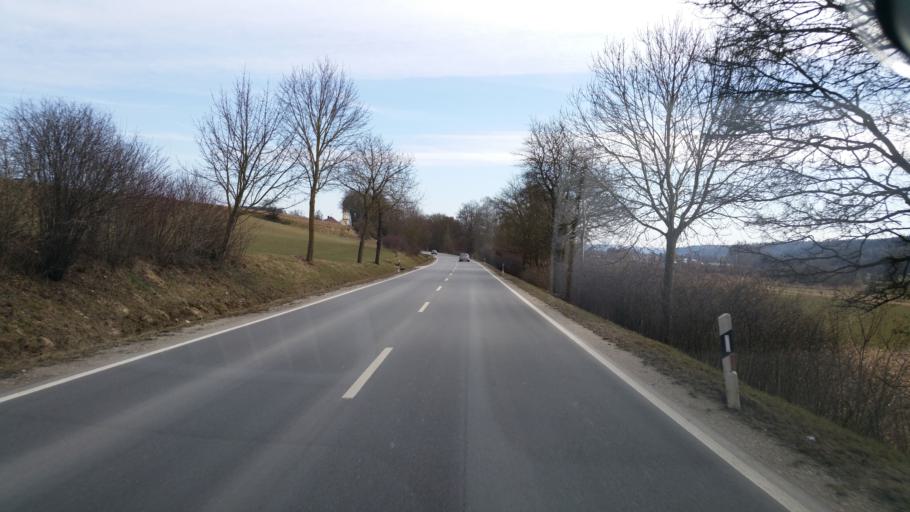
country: DE
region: Bavaria
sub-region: Lower Bavaria
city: Weihmichl
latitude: 48.5876
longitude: 12.0516
